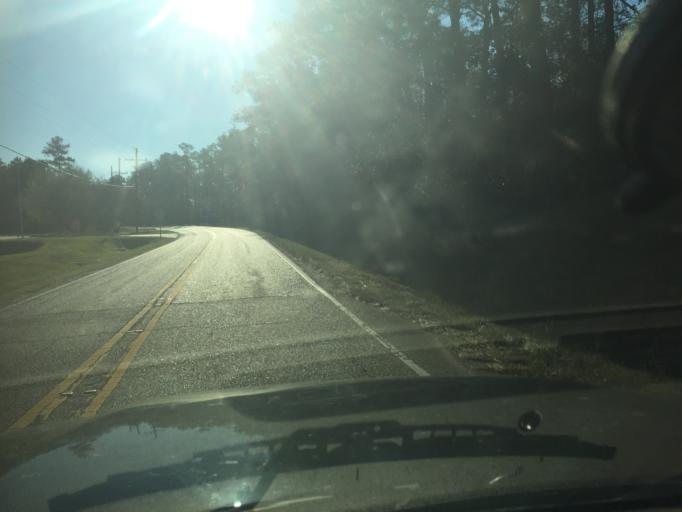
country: US
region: Louisiana
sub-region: Saint Tammany Parish
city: Slidell
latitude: 30.2437
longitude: -89.7593
